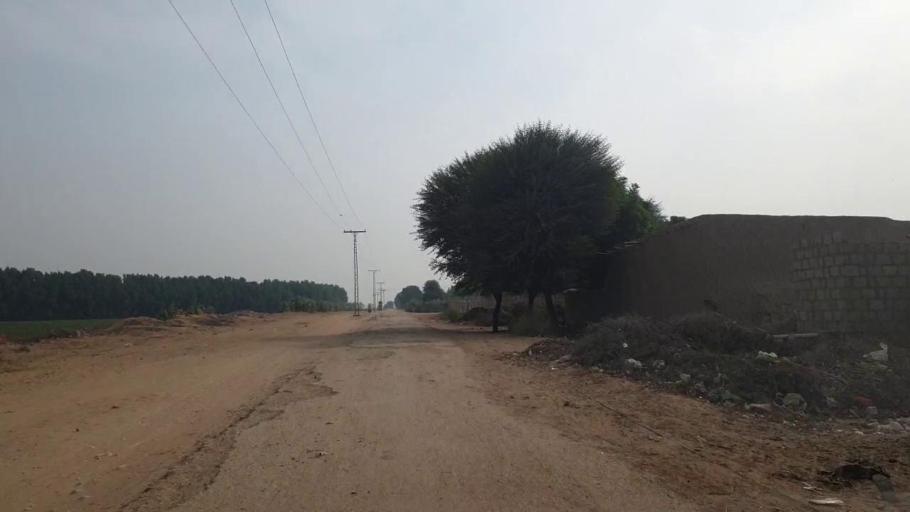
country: PK
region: Sindh
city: Sann
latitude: 26.0306
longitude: 68.1370
